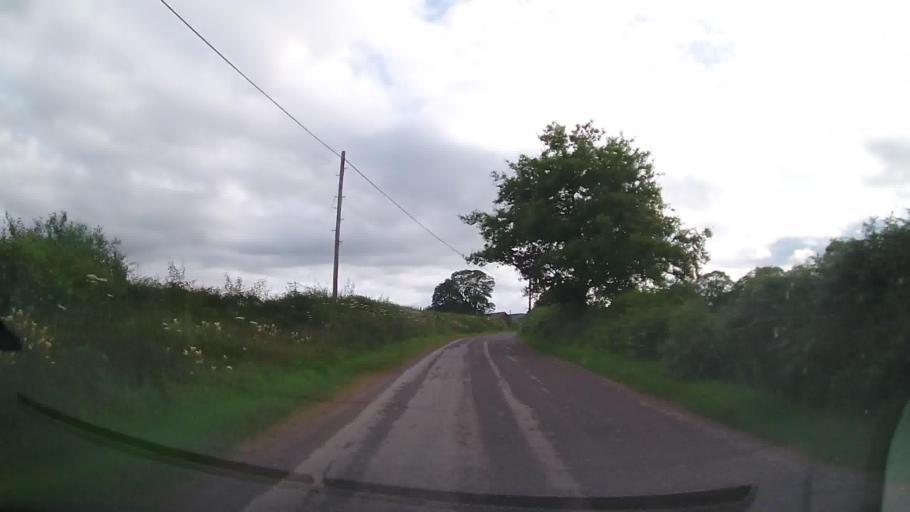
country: GB
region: England
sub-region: Shropshire
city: Whitchurch
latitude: 52.9295
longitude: -2.7245
